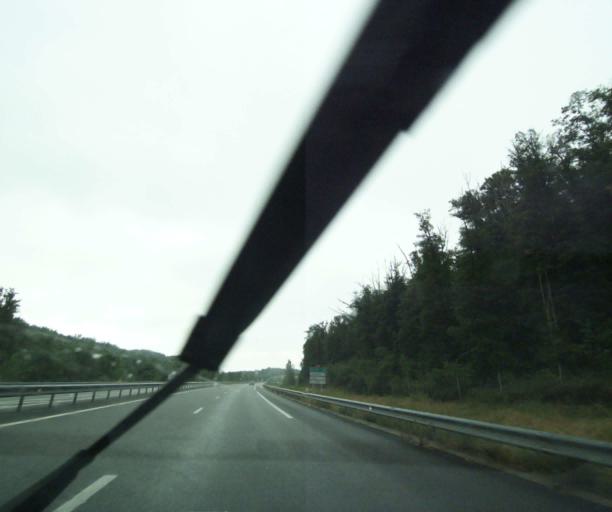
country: FR
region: Midi-Pyrenees
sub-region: Departement du Tarn
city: Le Garric
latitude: 43.9987
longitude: 2.1715
